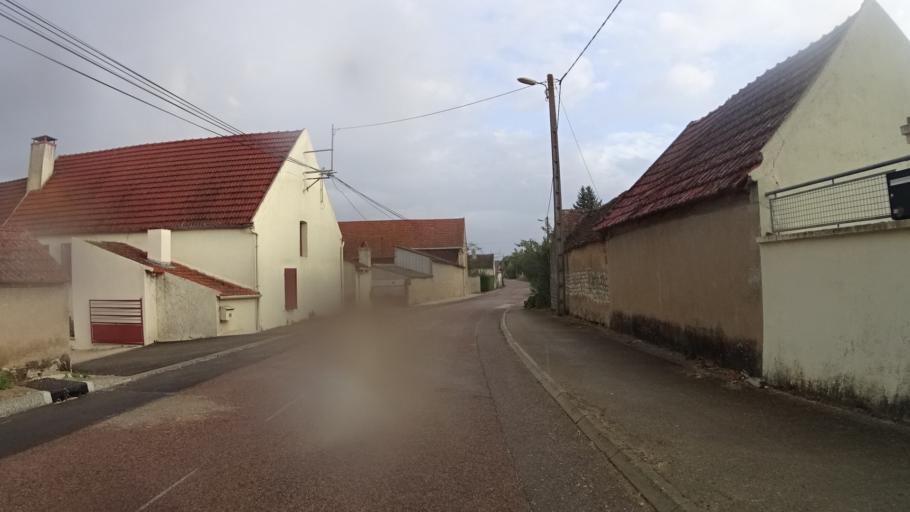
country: FR
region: Bourgogne
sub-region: Departement de Saone-et-Loire
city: Verdun-sur-le-Doubs
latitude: 46.9590
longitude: 5.0276
